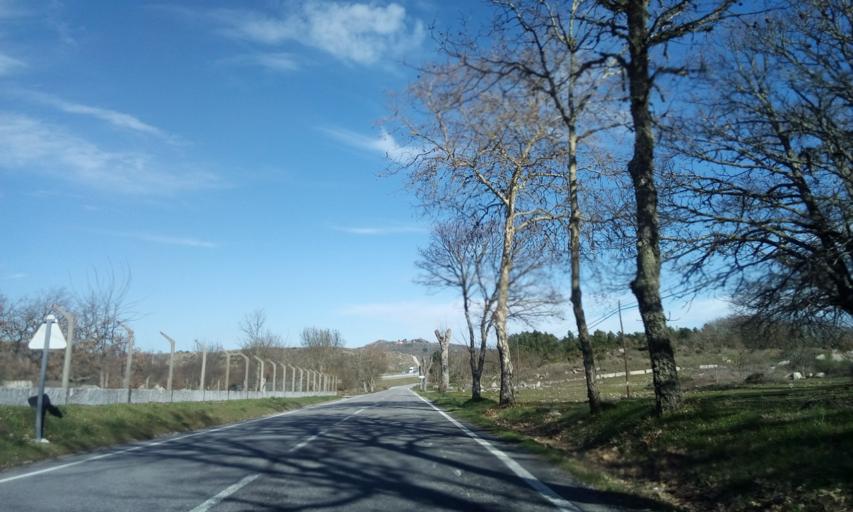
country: PT
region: Guarda
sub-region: Guarda
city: Sequeira
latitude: 40.5803
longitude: -7.1650
